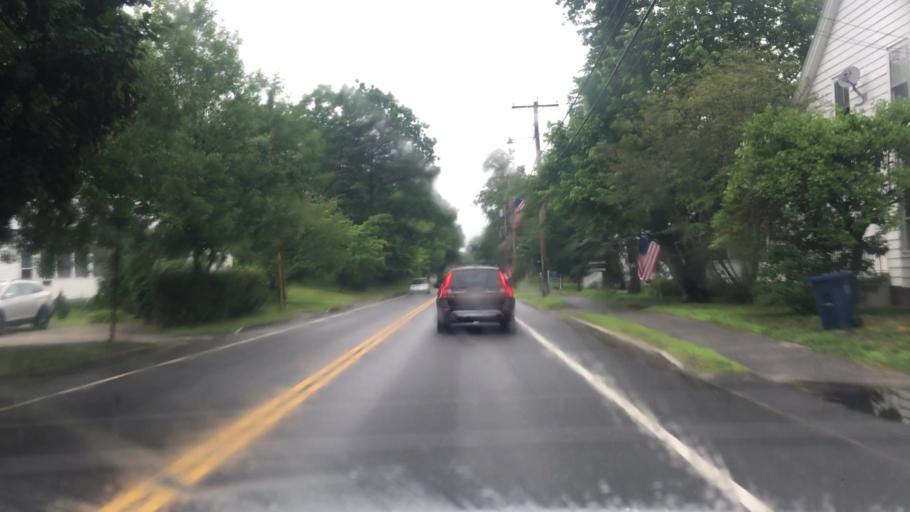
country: US
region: Maine
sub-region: Sagadahoc County
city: Topsham
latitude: 43.9300
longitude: -69.9643
